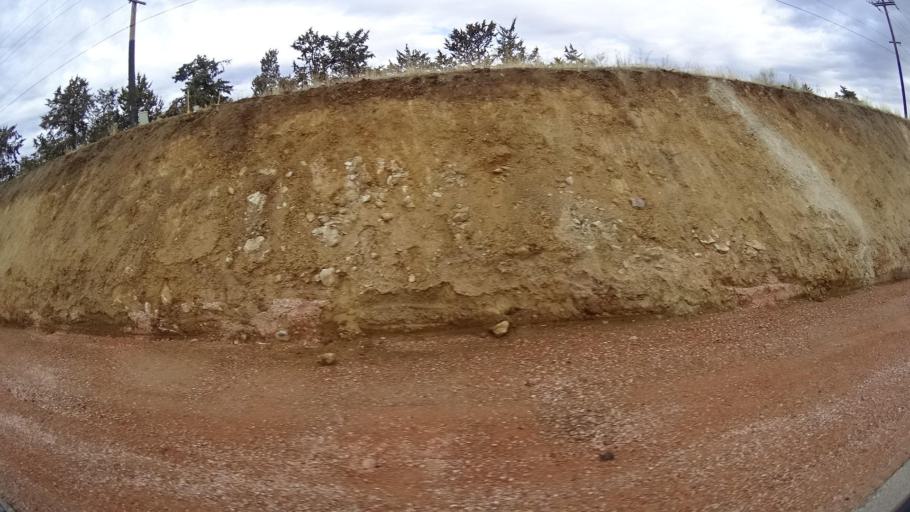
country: US
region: California
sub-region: Kern County
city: Golden Hills
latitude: 35.1145
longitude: -118.5285
